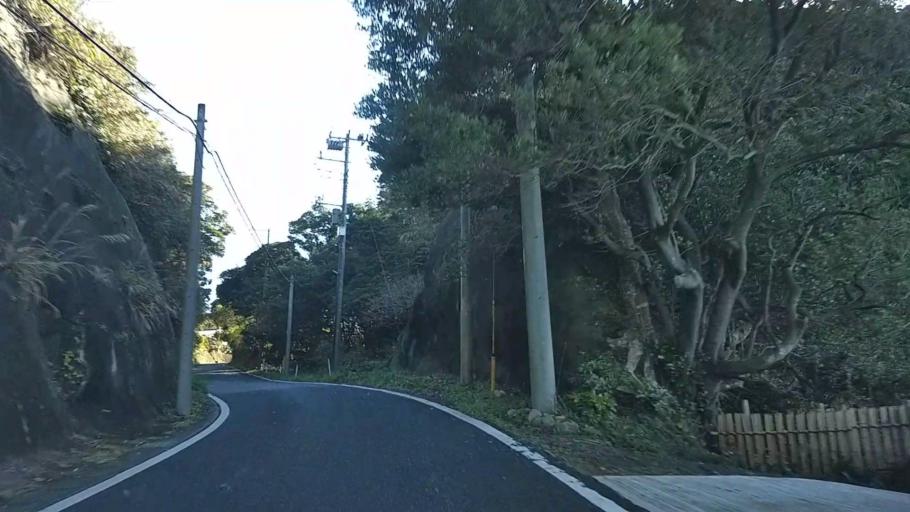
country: JP
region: Chiba
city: Futtsu
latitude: 35.2438
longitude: 139.8701
